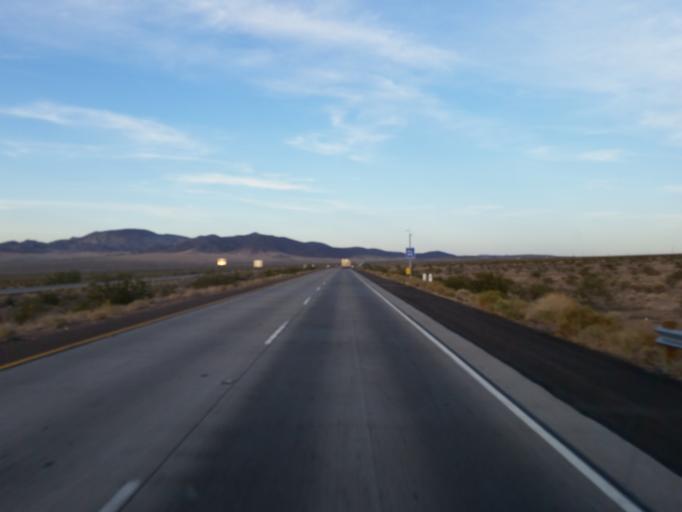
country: US
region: California
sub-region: San Bernardino County
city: Twentynine Palms
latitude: 34.7261
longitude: -116.1457
